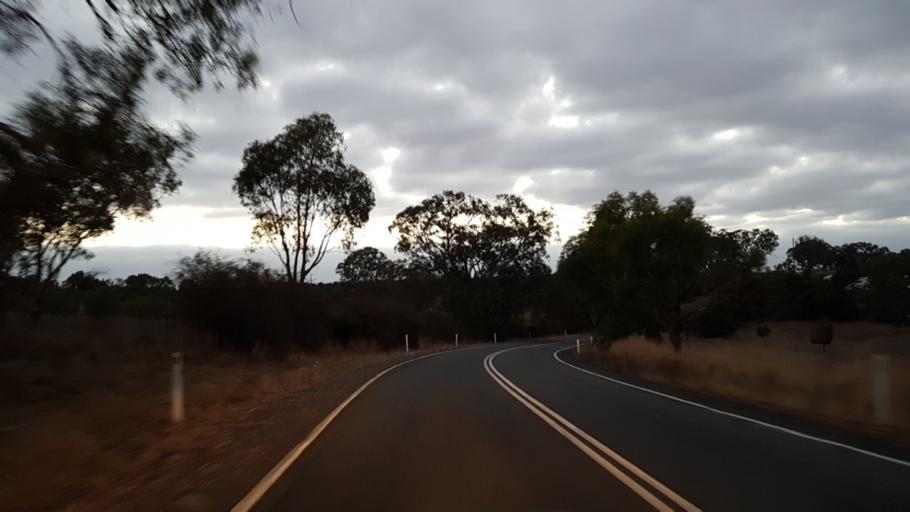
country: AU
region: South Australia
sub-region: Mount Barker
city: Nairne
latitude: -35.0304
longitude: 138.9567
